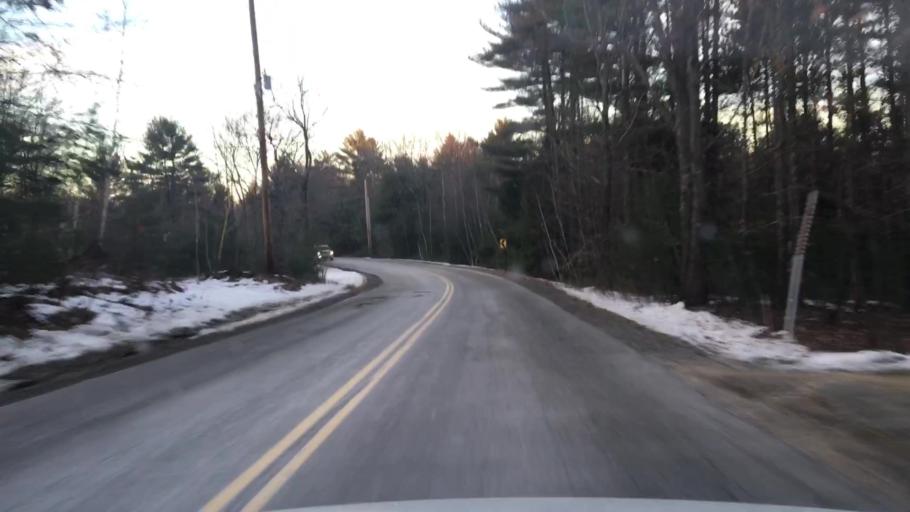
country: US
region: Maine
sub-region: York County
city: Lebanon
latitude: 43.3376
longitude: -70.8639
